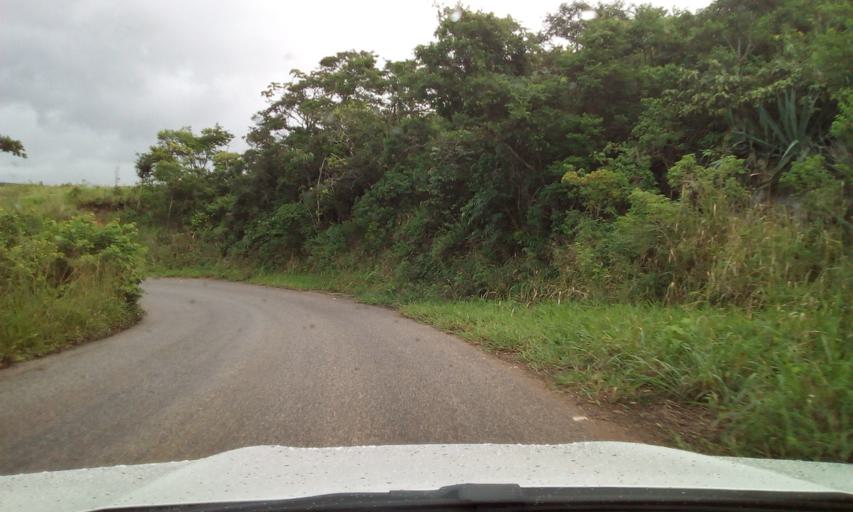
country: BR
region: Paraiba
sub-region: Areia
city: Areia
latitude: -6.9026
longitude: -35.6477
